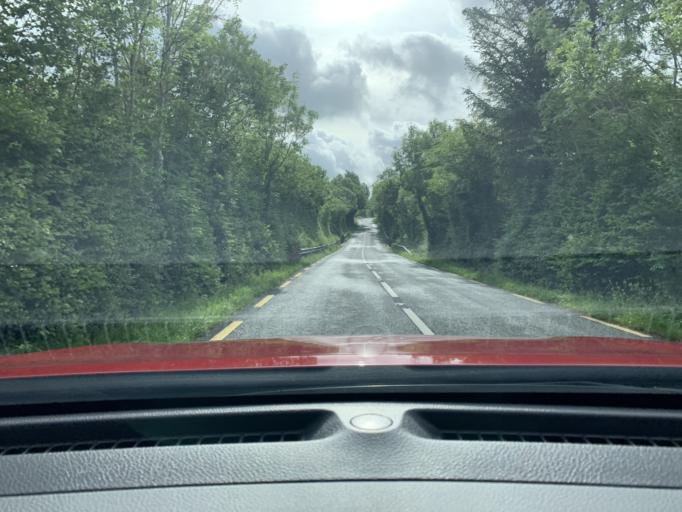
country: IE
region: Connaught
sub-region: Sligo
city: Sligo
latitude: 54.3267
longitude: -8.3478
